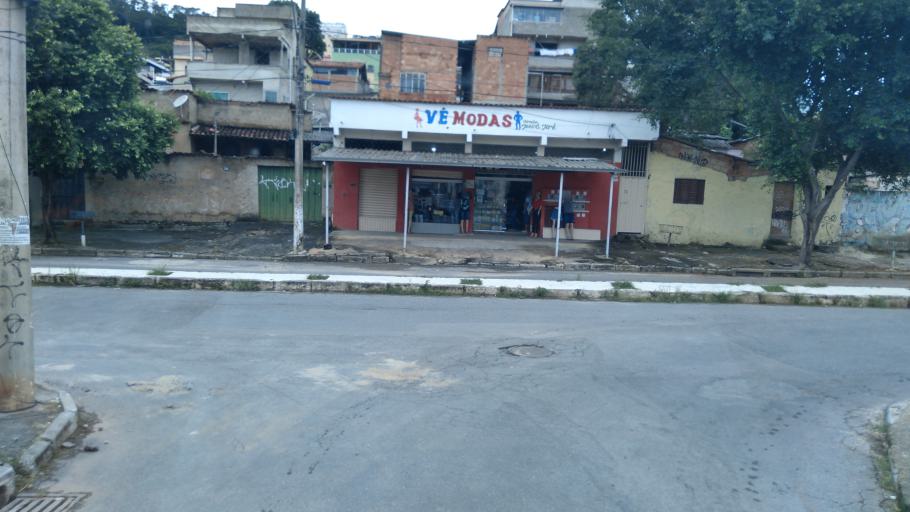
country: BR
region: Minas Gerais
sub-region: Belo Horizonte
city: Belo Horizonte
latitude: -19.8769
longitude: -43.8950
